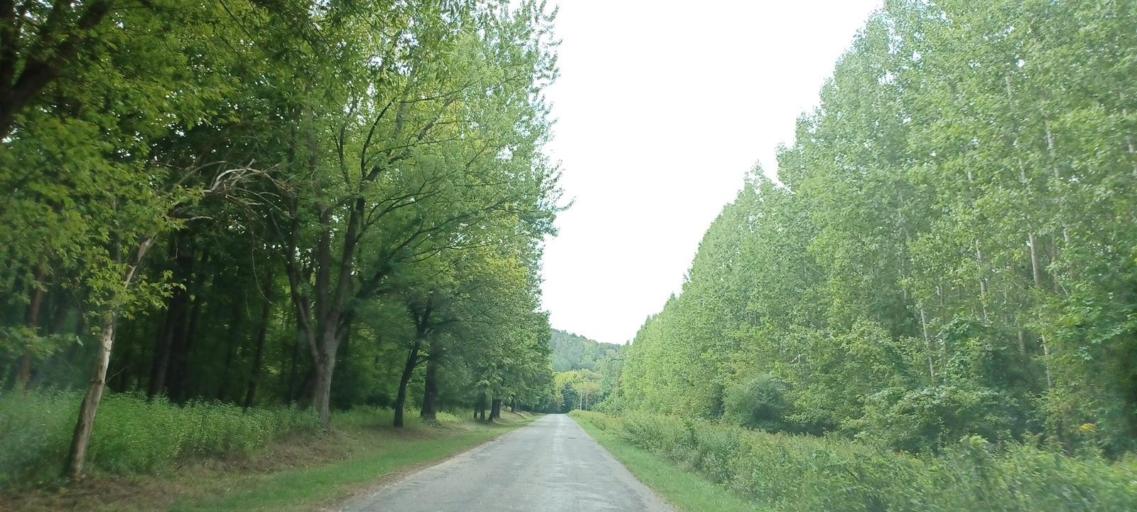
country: HU
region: Tolna
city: Szentgalpuszta
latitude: 46.3488
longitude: 18.6198
